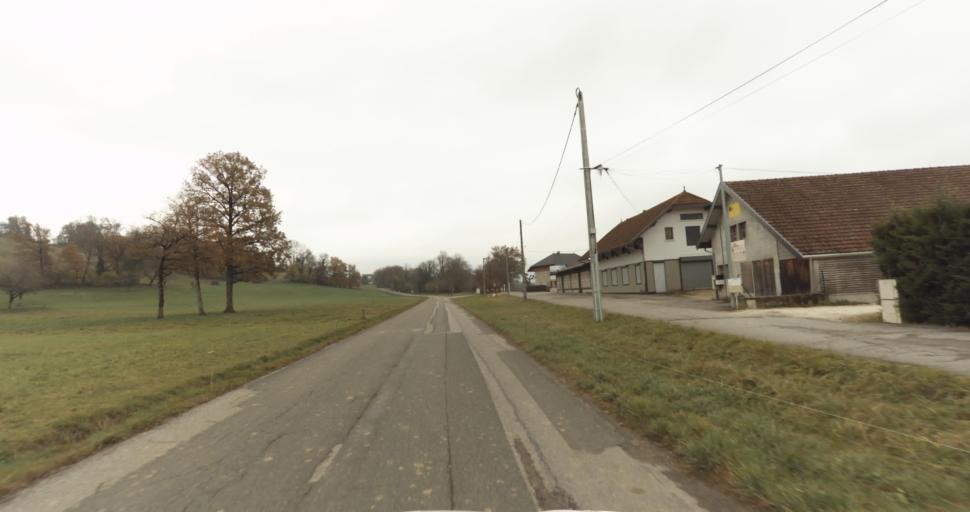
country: FR
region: Rhone-Alpes
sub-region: Departement de la Haute-Savoie
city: Alby-sur-Cheran
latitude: 45.8035
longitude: 6.0329
